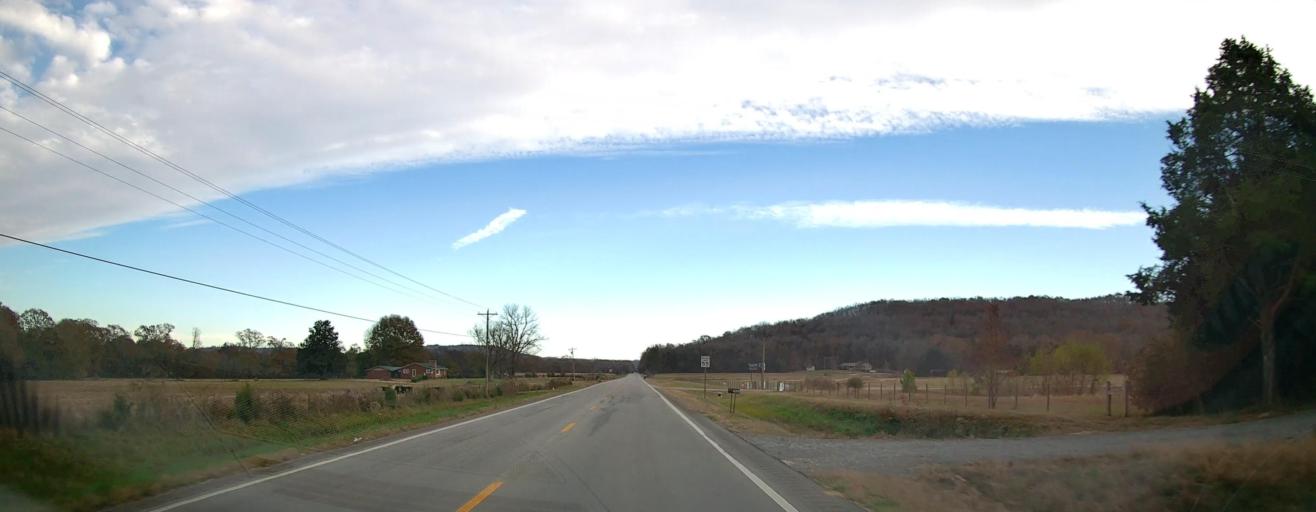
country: US
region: Alabama
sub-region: Marshall County
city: Arab
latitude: 34.4032
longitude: -86.6867
